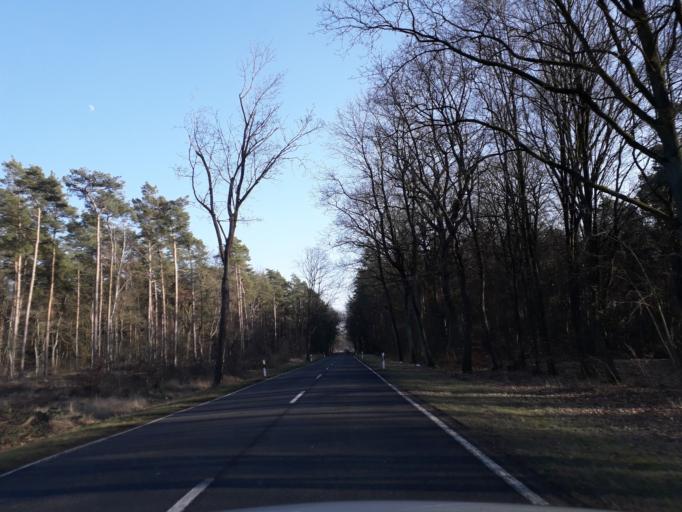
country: DE
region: Brandenburg
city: Brieselang
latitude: 52.6179
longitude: 12.9926
